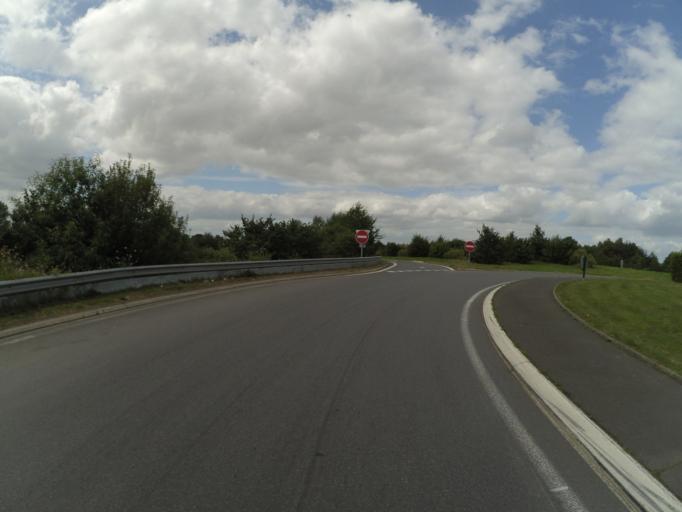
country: FR
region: Brittany
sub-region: Departement des Cotes-d'Armor
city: Plestan
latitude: 48.4179
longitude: -2.4431
